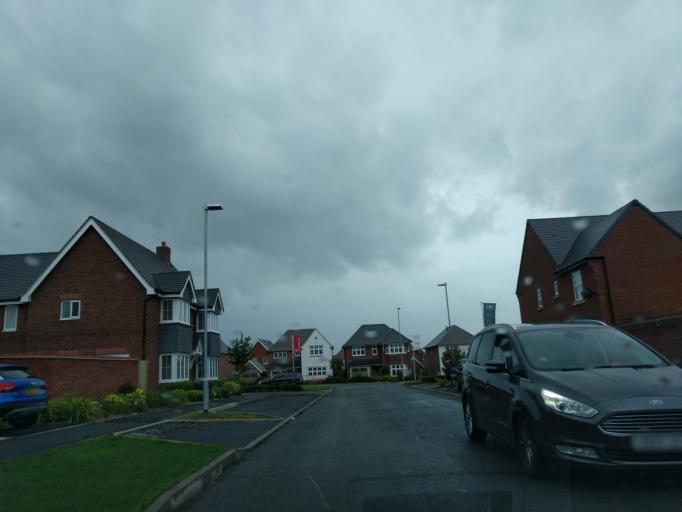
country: GB
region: England
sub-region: Staffordshire
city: Stafford
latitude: 52.8080
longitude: -2.0788
